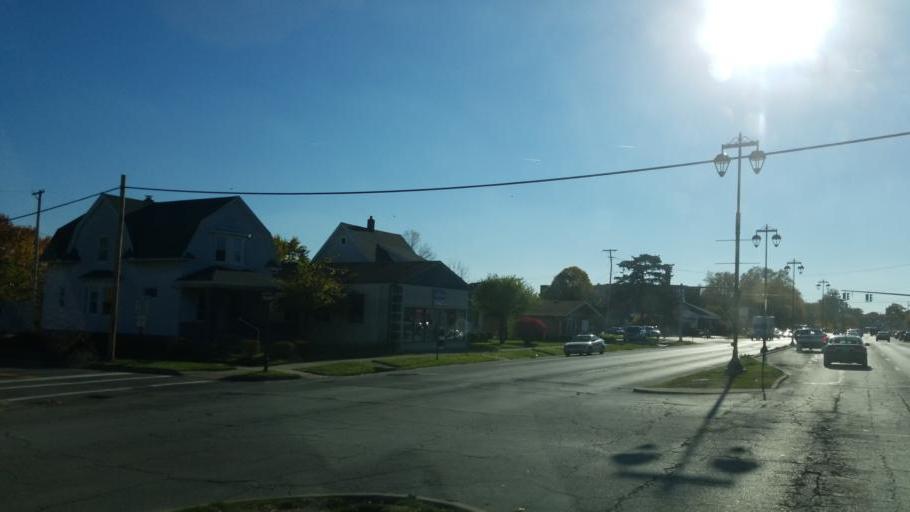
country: US
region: Ohio
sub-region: Wood County
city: Rossford
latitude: 41.6114
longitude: -83.5571
